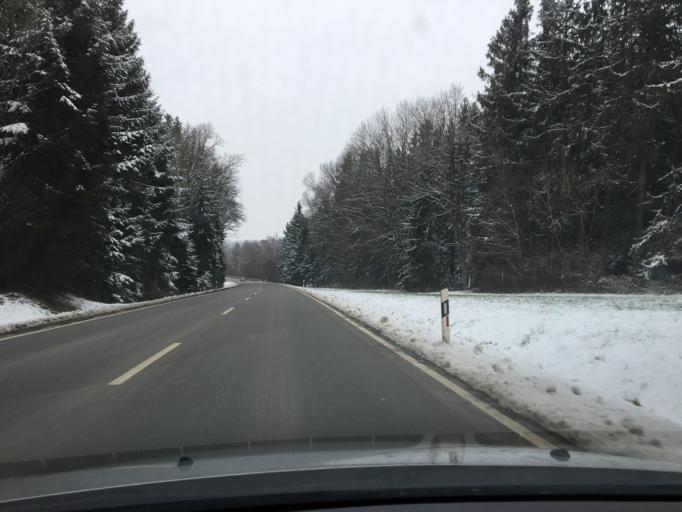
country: DE
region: Bavaria
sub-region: Lower Bavaria
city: Vilsbiburg
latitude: 48.4359
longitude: 12.3795
